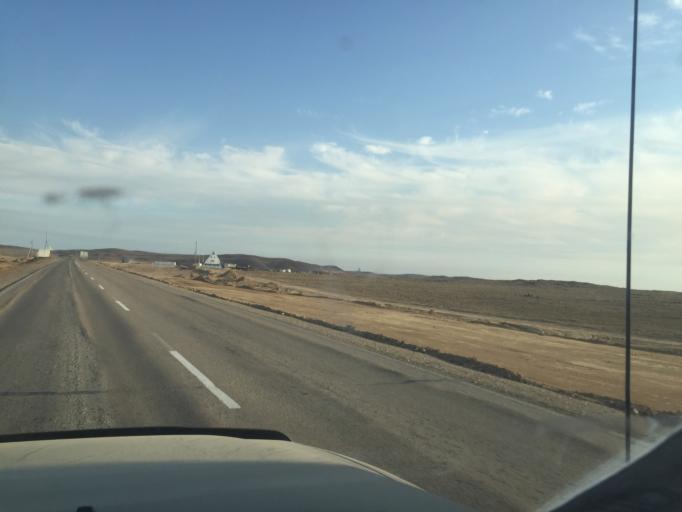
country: KZ
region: Zhambyl
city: Mynaral
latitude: 45.4531
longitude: 73.5975
